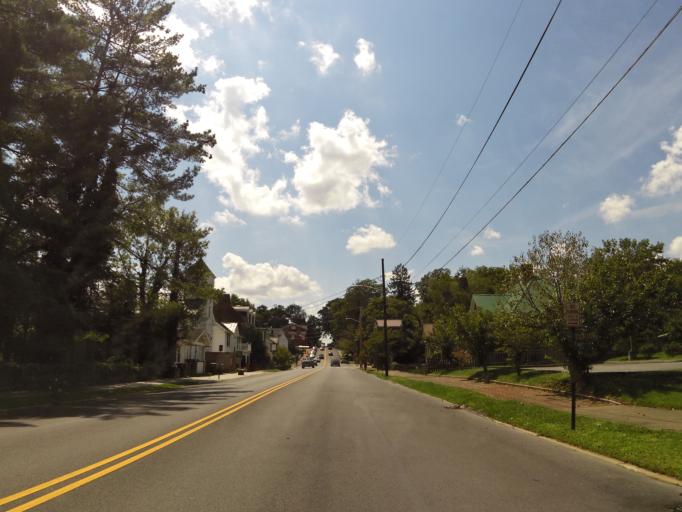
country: US
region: Virginia
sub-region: Washington County
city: Abingdon
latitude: 36.7135
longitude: -81.9662
